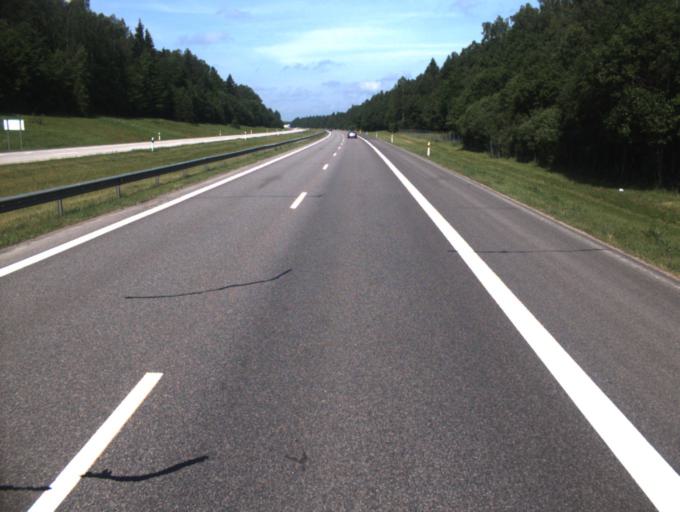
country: LT
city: Rietavas
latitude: 55.6902
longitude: 21.6829
